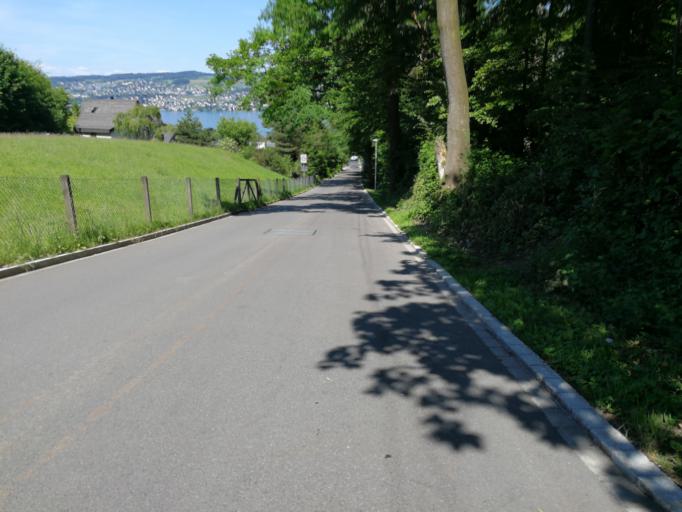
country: CH
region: Zurich
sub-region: Bezirk Horgen
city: Horgen / Allmend
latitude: 47.2498
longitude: 8.6084
